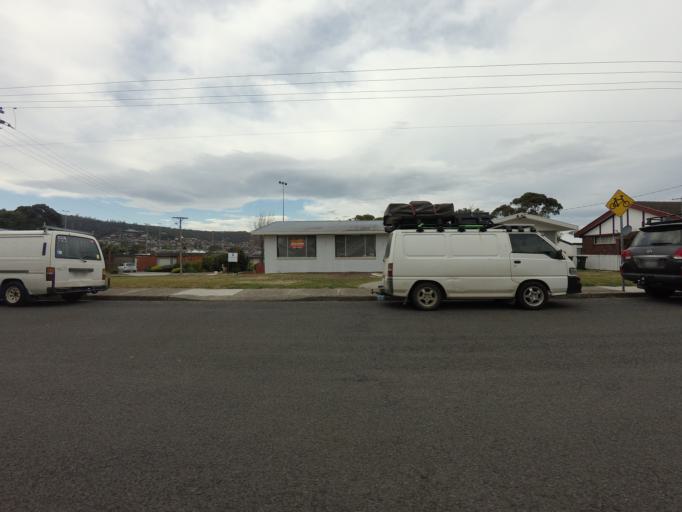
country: AU
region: Tasmania
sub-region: Clarence
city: Howrah
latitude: -42.8796
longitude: 147.3909
